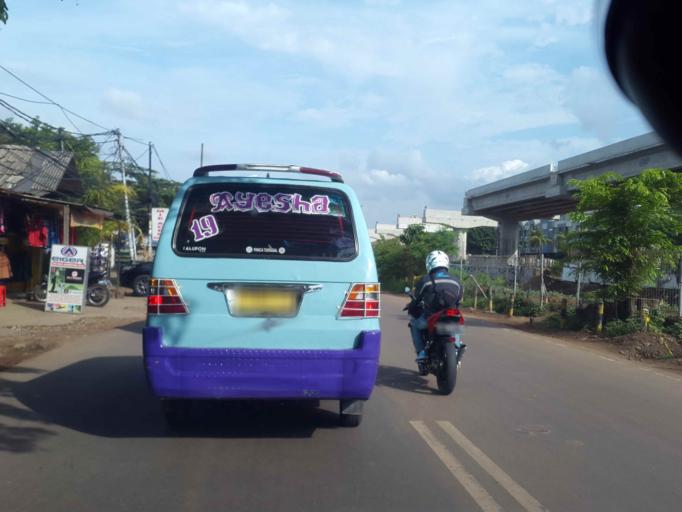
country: ID
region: Jakarta Raya
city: Jakarta
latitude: -6.2472
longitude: 106.9095
